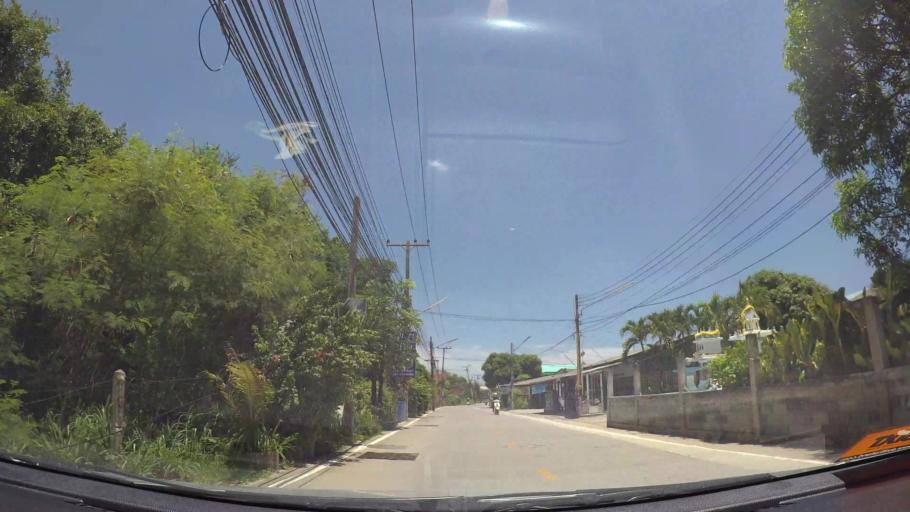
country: TH
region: Chon Buri
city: Si Racha
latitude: 13.1133
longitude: 100.9330
